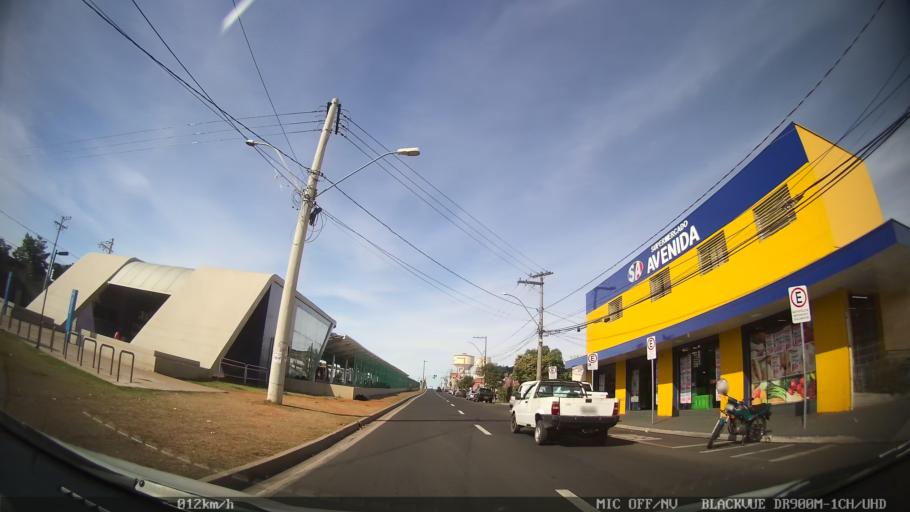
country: BR
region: Sao Paulo
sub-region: Piracicaba
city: Piracicaba
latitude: -22.7517
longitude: -47.6489
